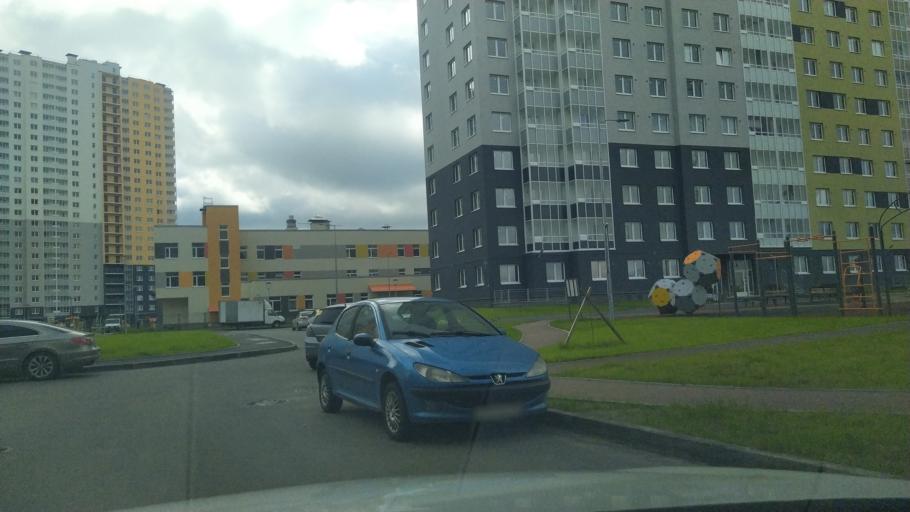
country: RU
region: St.-Petersburg
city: Krasnogvargeisky
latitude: 60.0155
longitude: 30.4812
